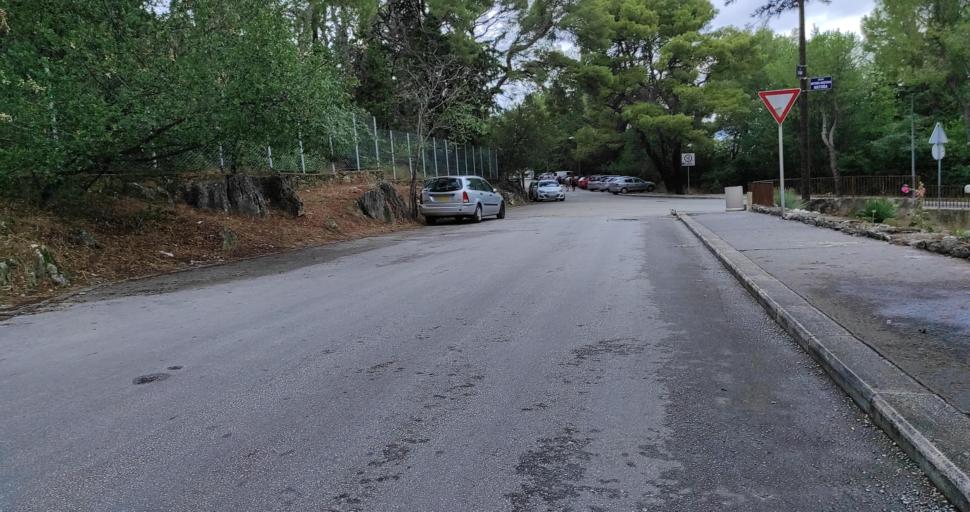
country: HR
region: Splitsko-Dalmatinska
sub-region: Grad Split
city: Split
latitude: 43.5132
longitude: 16.4233
